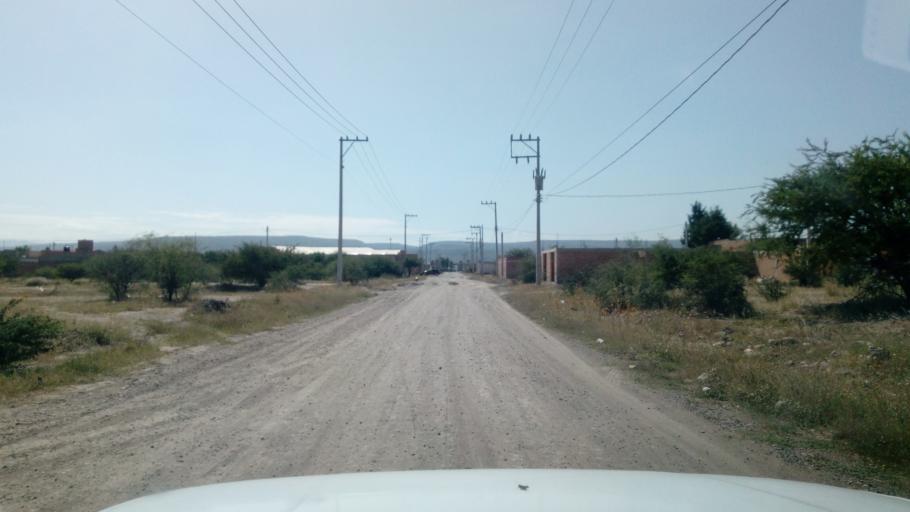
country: MX
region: Durango
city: Victoria de Durango
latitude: 23.9819
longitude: -104.6809
